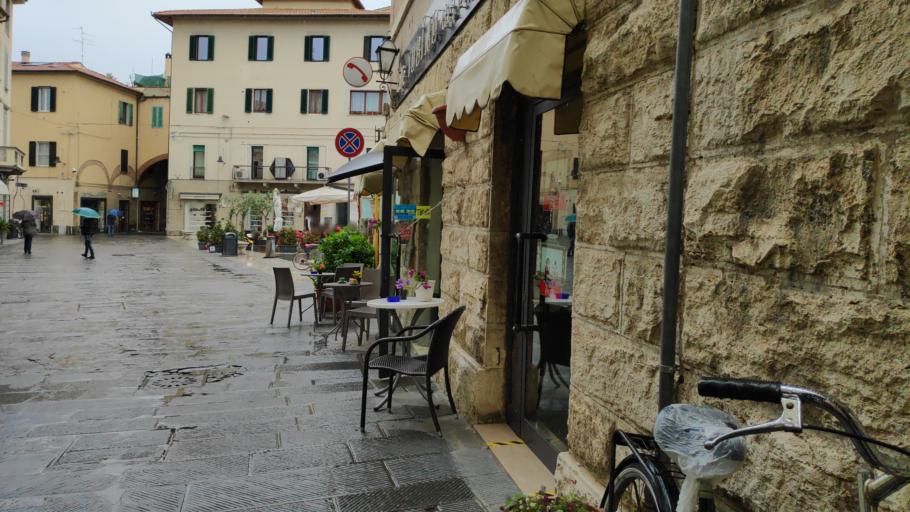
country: IT
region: Tuscany
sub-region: Provincia di Grosseto
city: Grosseto
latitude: 42.7590
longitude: 11.1142
